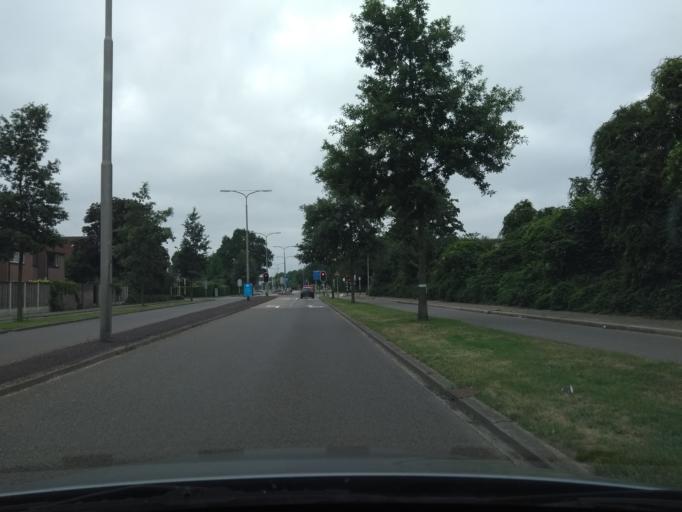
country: NL
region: Overijssel
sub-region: Gemeente Almelo
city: Almelo
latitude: 52.3791
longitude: 6.6727
